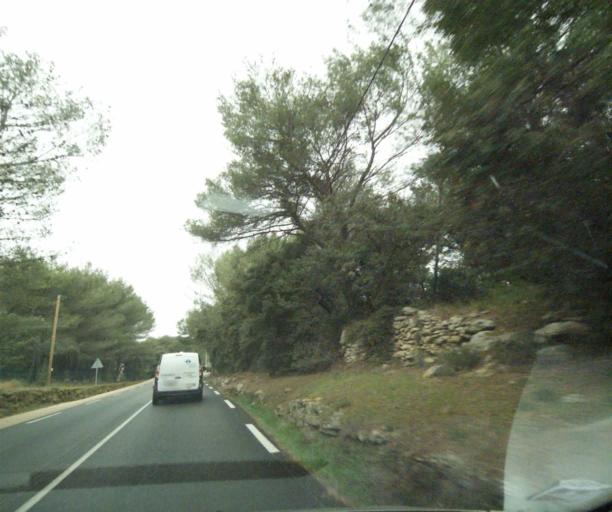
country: FR
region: Provence-Alpes-Cote d'Azur
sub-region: Departement des Bouches-du-Rhone
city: Rognes
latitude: 43.6641
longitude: 5.3297
